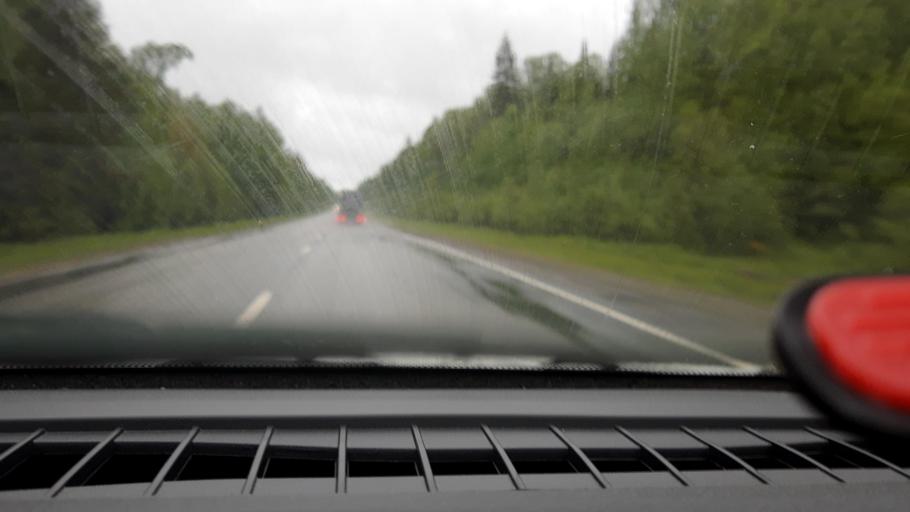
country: RU
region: Nizjnij Novgorod
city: Vladimirskoye
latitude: 56.9332
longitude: 45.0710
